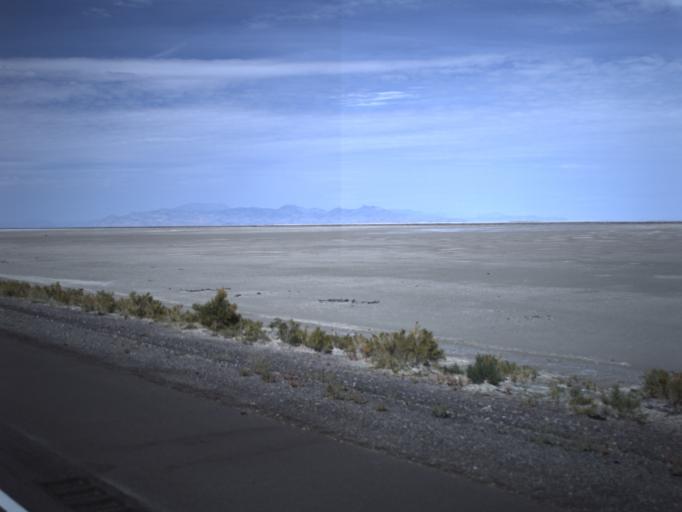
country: US
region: Utah
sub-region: Tooele County
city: Wendover
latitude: 40.7287
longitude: -113.3558
